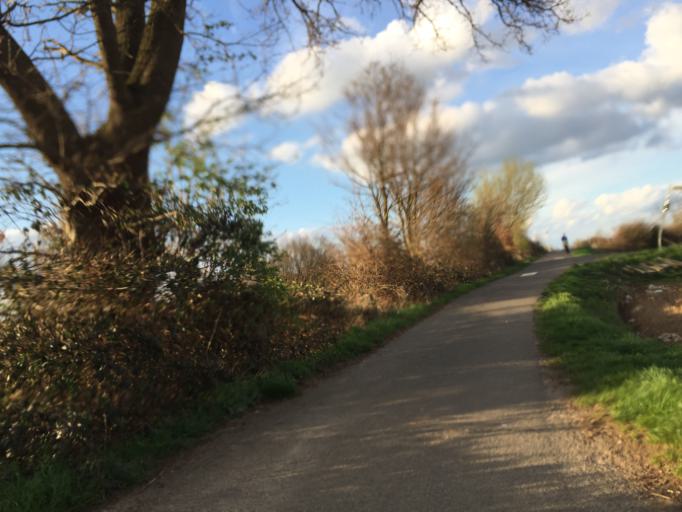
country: DE
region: North Rhine-Westphalia
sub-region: Regierungsbezirk Koln
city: Bonn
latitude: 50.7283
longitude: 7.0568
